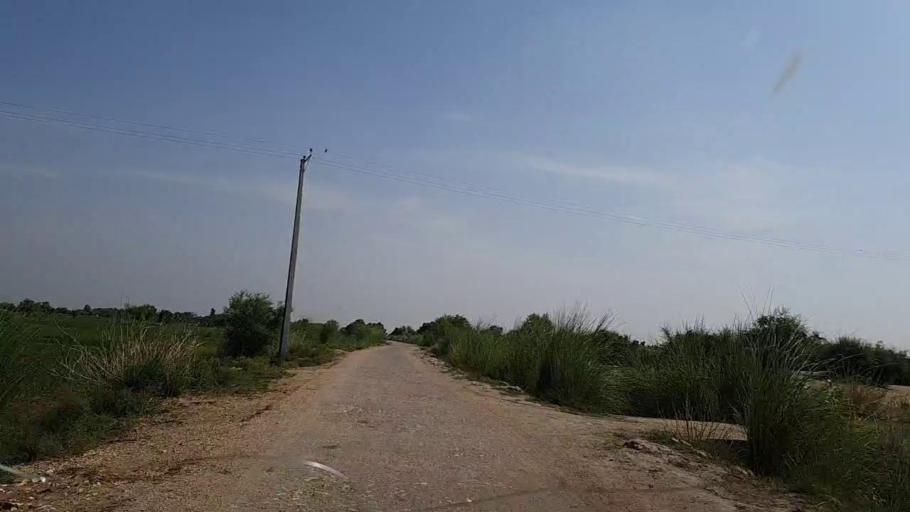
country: PK
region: Sindh
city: Khanpur
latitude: 27.7148
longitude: 69.3624
